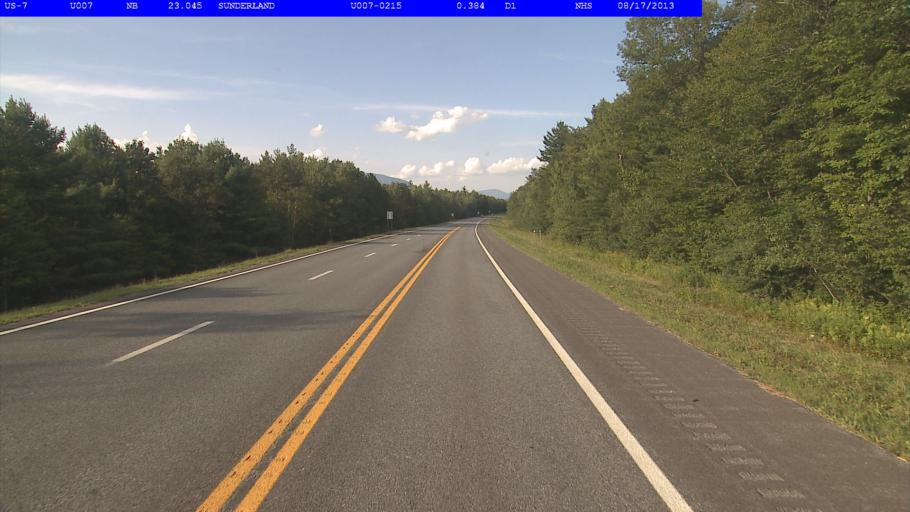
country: US
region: Vermont
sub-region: Bennington County
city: Arlington
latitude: 43.0312
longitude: -73.1386
